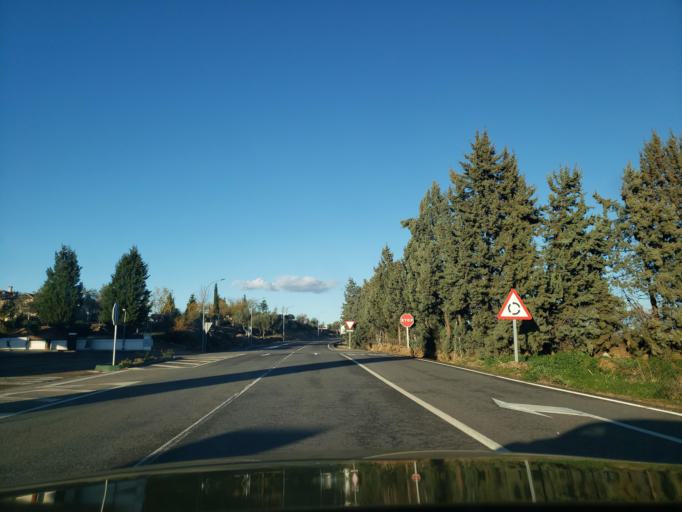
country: ES
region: Castille-La Mancha
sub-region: Province of Toledo
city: Cobisa
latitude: 39.8172
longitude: -4.0211
